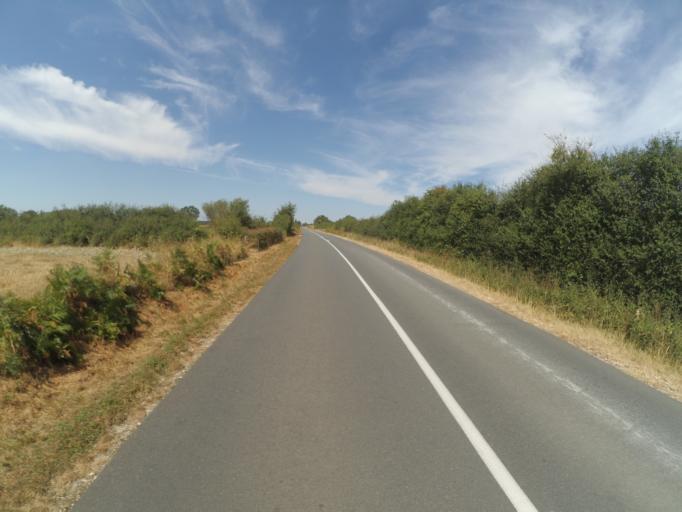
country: FR
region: Poitou-Charentes
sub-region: Departement de la Vienne
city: Availles-Limouzine
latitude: 46.1445
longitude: 0.5558
